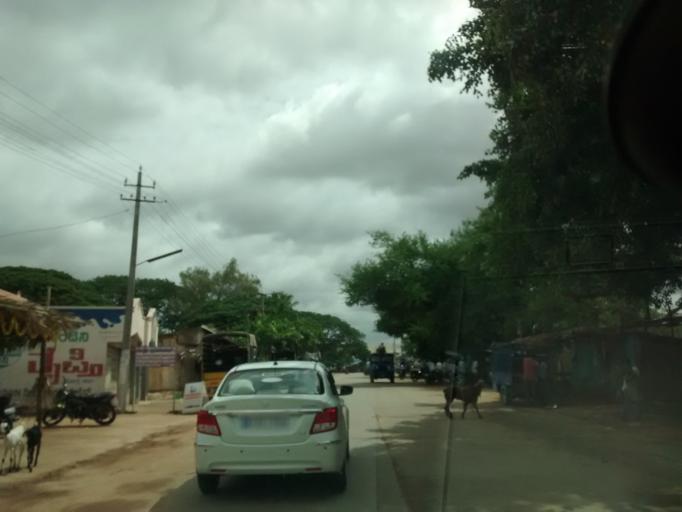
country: IN
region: Karnataka
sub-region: Tumkur
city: Kodigenahalli
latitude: 13.7188
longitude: 77.3862
